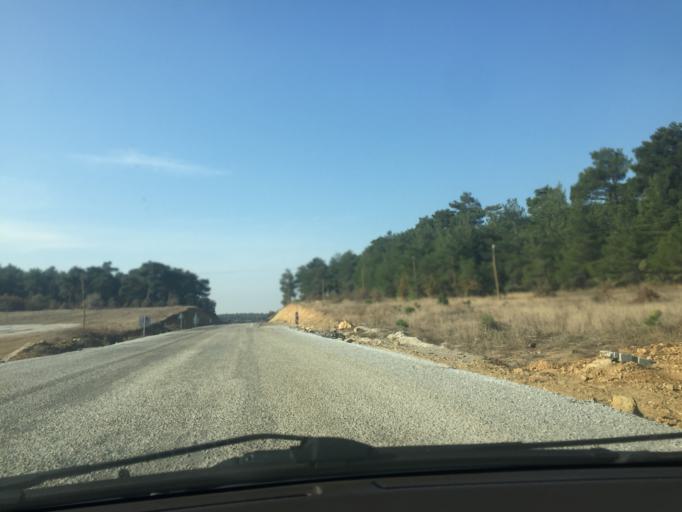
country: TR
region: Canakkale
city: Yigitler
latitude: 39.8914
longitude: 26.7169
